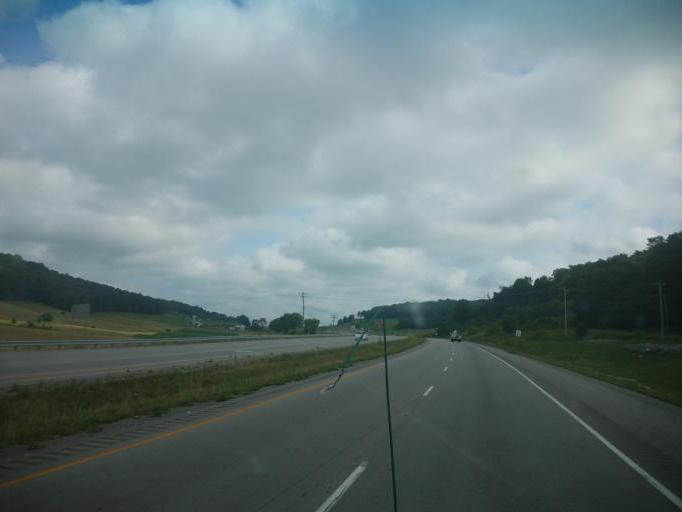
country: US
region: Kentucky
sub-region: Clinton County
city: Albany
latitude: 36.7302
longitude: -85.1343
